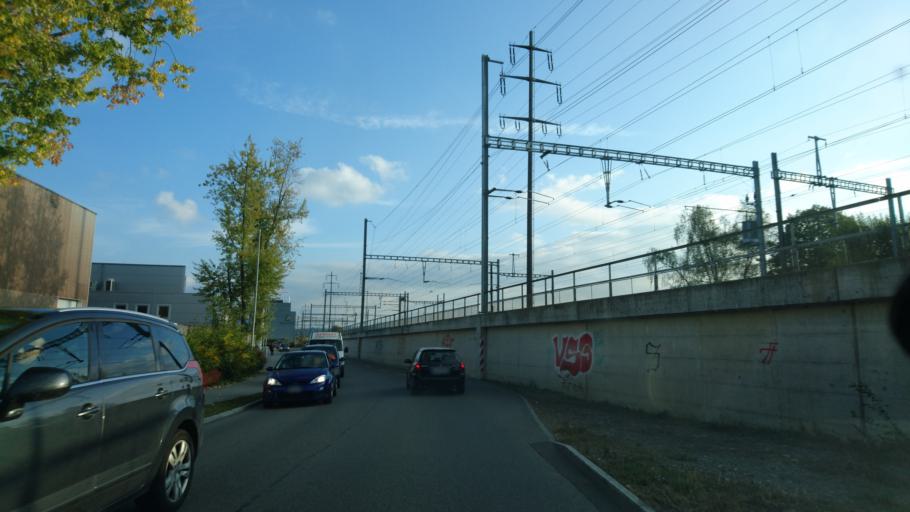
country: CH
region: Bern
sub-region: Bern-Mittelland District
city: Zollikofen
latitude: 46.9962
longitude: 7.4628
